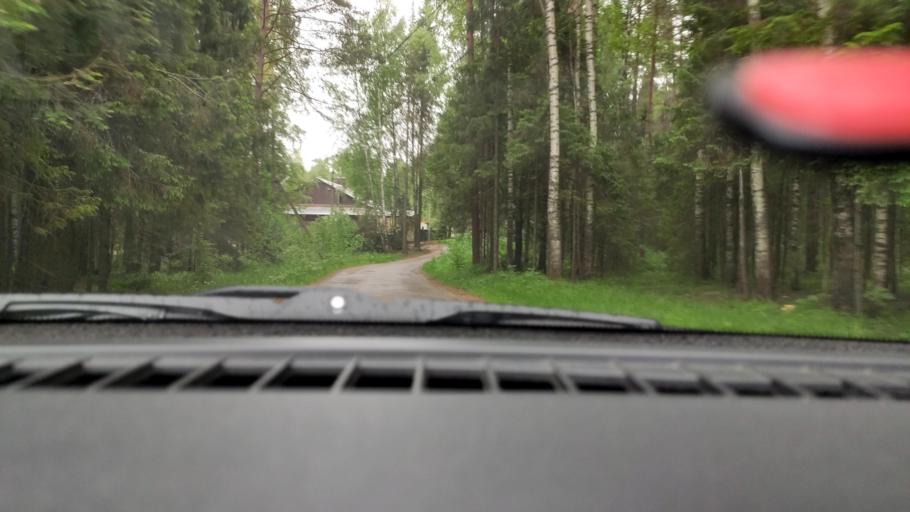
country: RU
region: Perm
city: Karagay
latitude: 58.2380
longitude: 54.8721
